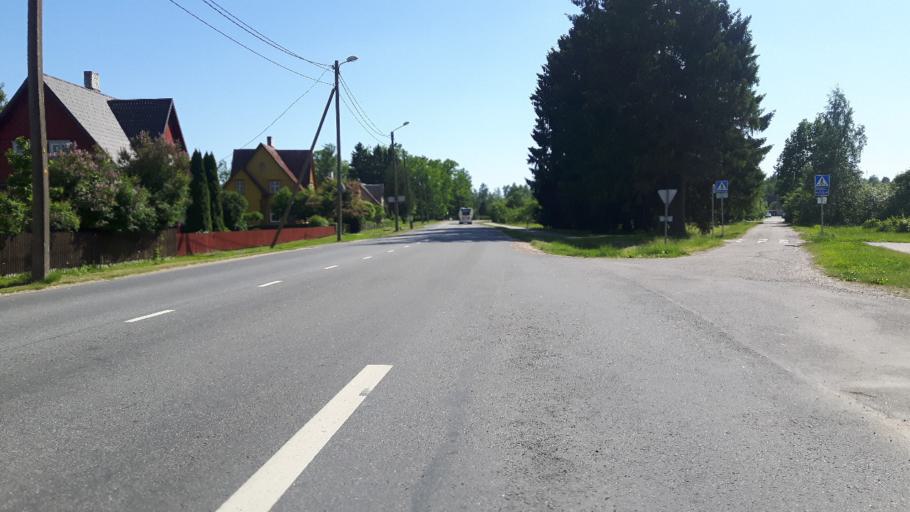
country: EE
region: Paernumaa
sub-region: Sindi linn
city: Sindi
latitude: 58.4021
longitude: 24.6464
